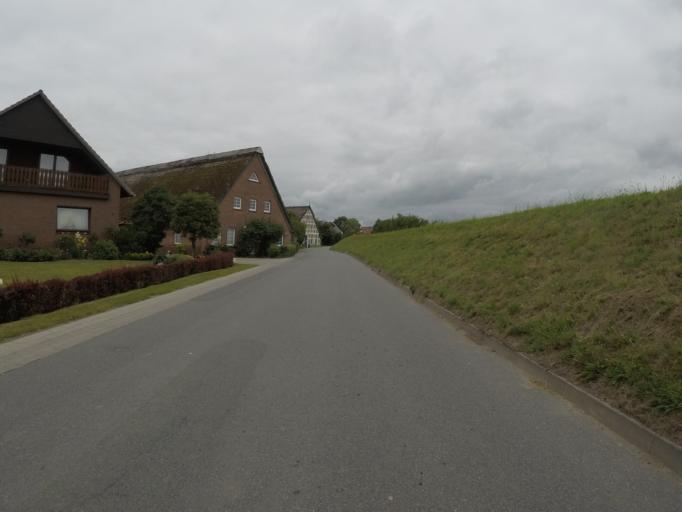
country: DE
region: Lower Saxony
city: Guderhandviertel
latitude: 53.5521
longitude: 9.6073
